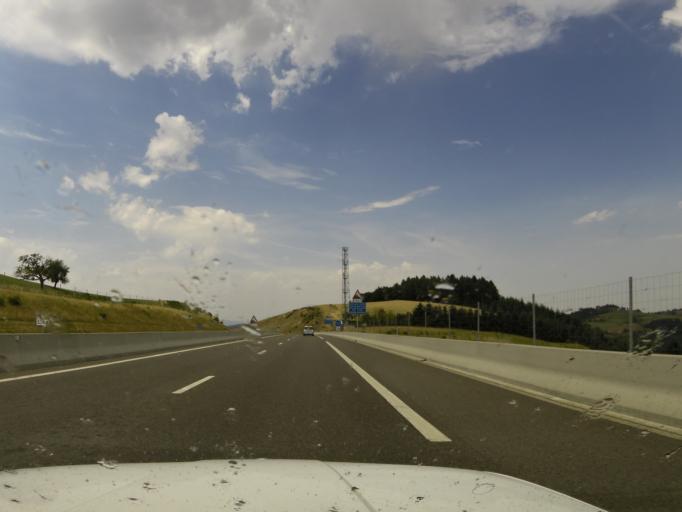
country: FR
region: Rhone-Alpes
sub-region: Departement de la Loire
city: Bussieres
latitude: 45.8679
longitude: 4.3008
